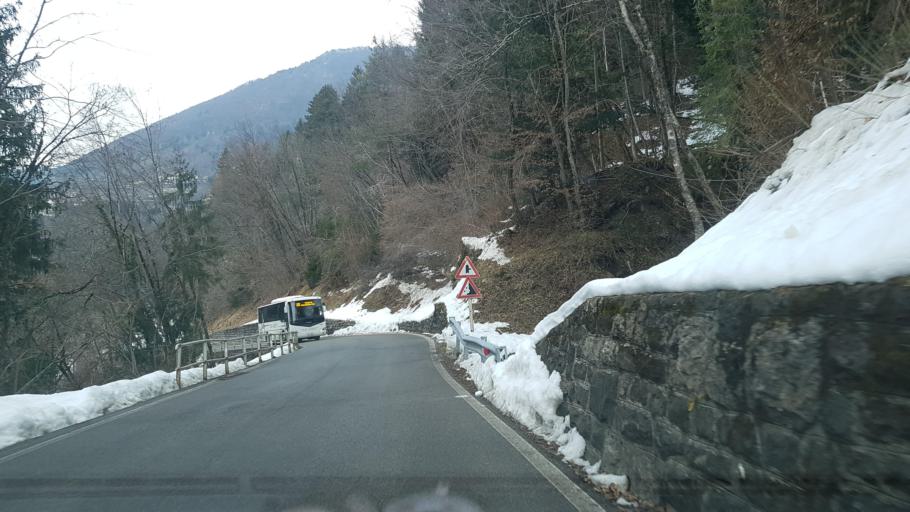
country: IT
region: Friuli Venezia Giulia
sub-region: Provincia di Udine
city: Lauco
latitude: 46.4248
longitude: 12.9227
